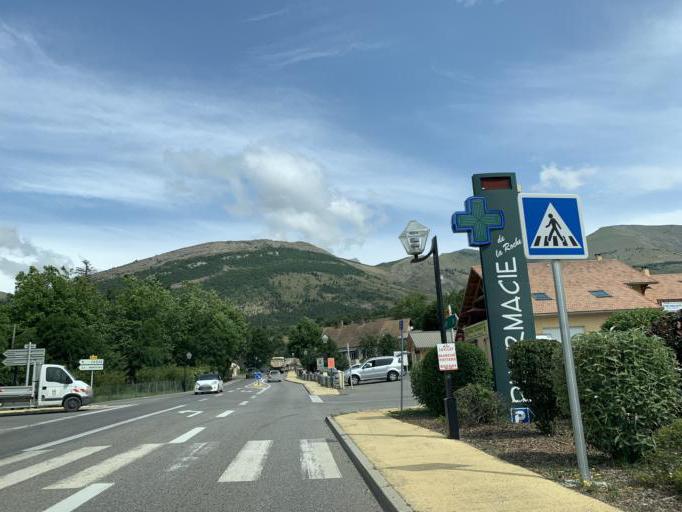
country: FR
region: Provence-Alpes-Cote d'Azur
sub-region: Departement des Hautes-Alpes
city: La Roche-des-Arnauds
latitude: 44.5599
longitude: 5.9568
